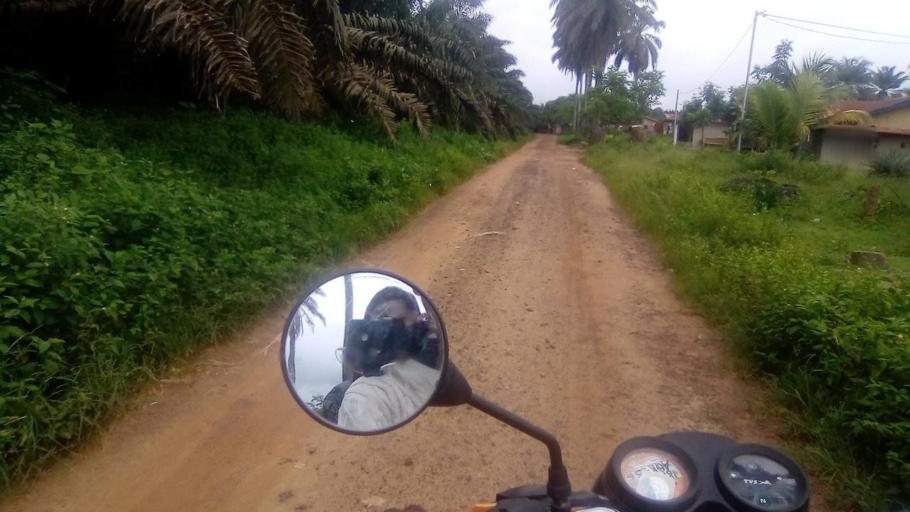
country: SL
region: Southern Province
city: Tongole
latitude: 7.4319
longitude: -11.8447
